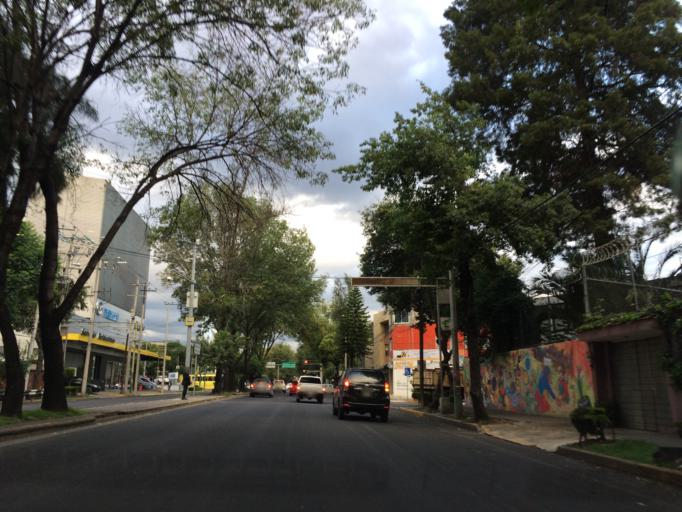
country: MX
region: Mexico City
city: Colonia del Valle
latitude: 19.3684
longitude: -99.1605
